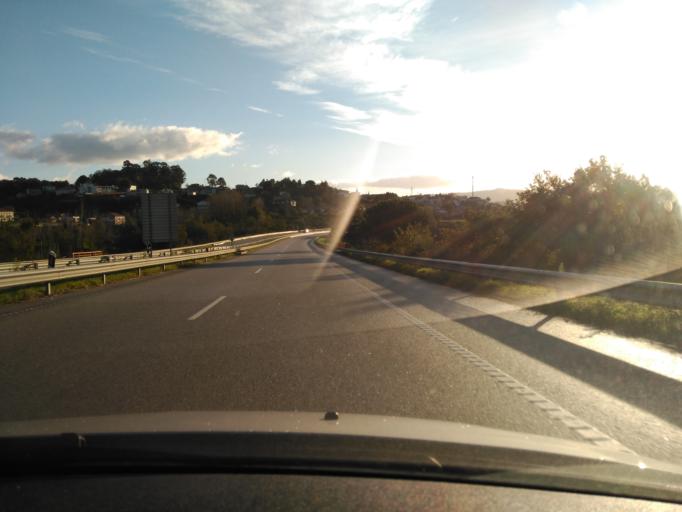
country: PT
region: Braga
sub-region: Fafe
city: Aroes
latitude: 41.4567
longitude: -8.2234
